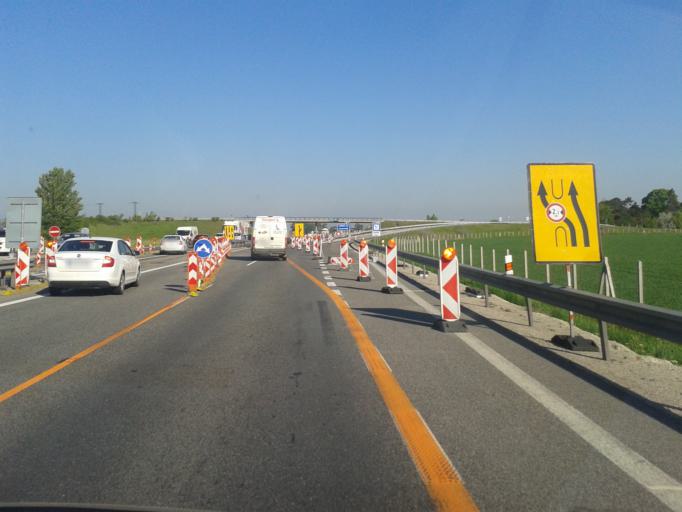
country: SK
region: Trnavsky
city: Sladkovicovo
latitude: 48.2993
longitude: 17.6623
